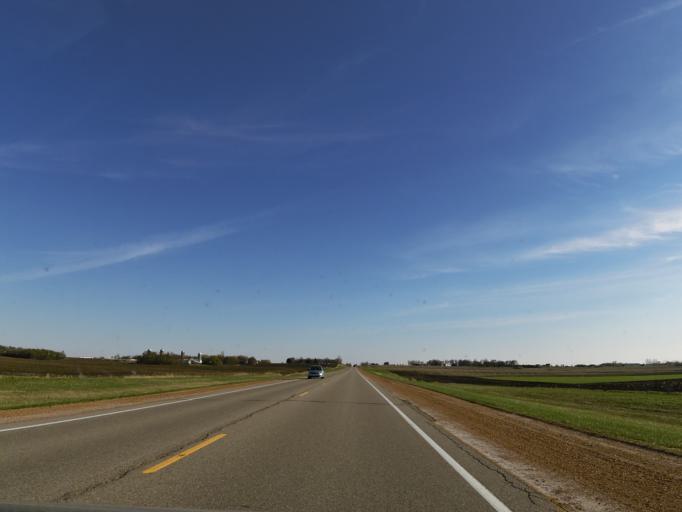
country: US
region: Minnesota
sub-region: Le Sueur County
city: New Prague
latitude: 44.6129
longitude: -93.5015
